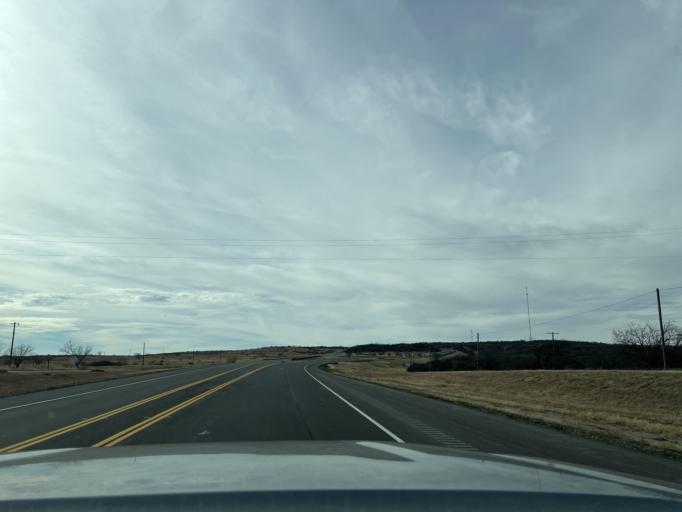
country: US
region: Texas
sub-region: Shackelford County
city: Albany
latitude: 32.7050
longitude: -99.4072
